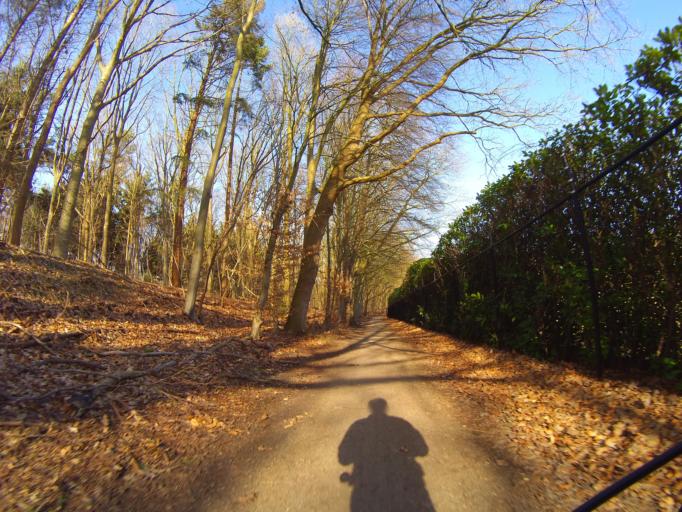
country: NL
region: North Holland
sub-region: Gemeente Naarden
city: Naarden
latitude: 52.2975
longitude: 5.1870
